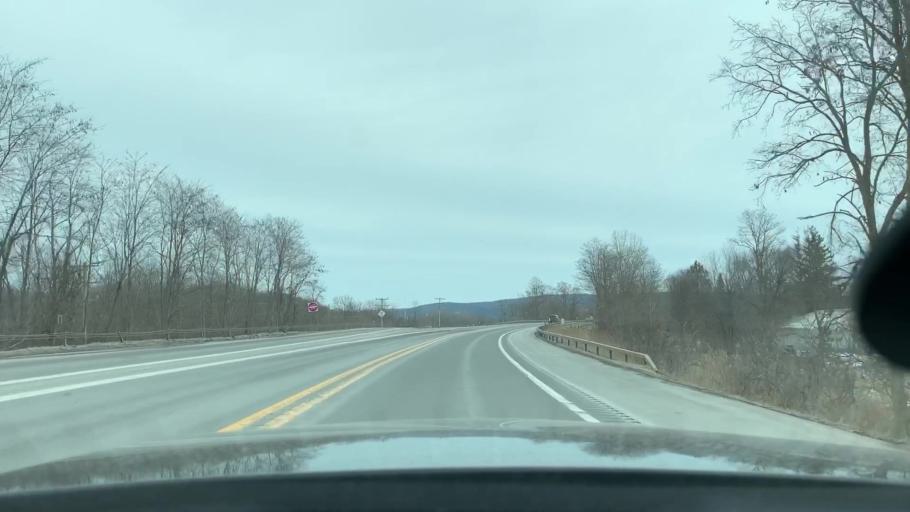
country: US
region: New York
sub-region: Herkimer County
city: Ilion
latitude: 43.0218
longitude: -75.0345
